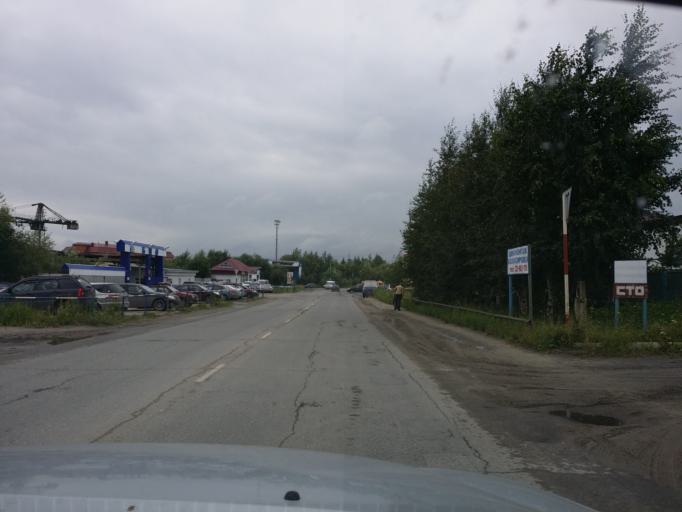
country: RU
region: Khanty-Mansiyskiy Avtonomnyy Okrug
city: Nizhnevartovsk
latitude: 60.9535
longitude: 76.5558
